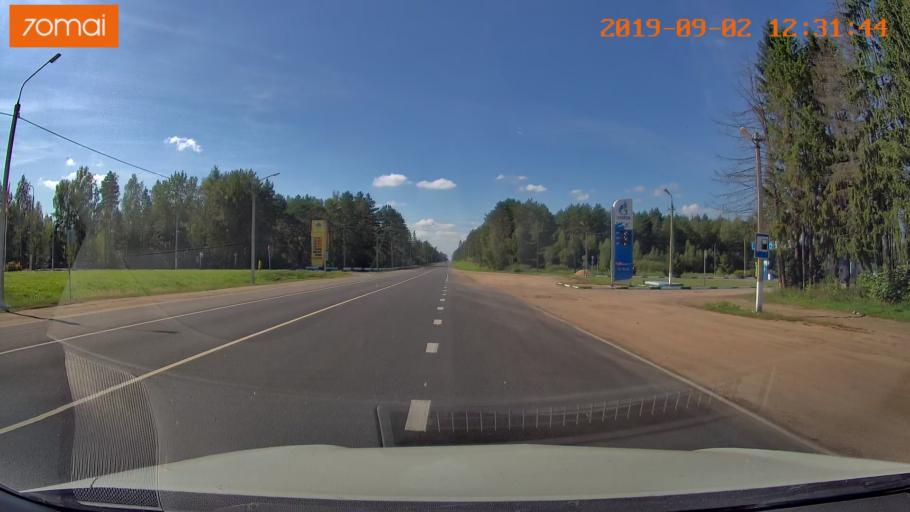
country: RU
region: Smolensk
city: Shumyachi
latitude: 53.8227
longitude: 32.4442
